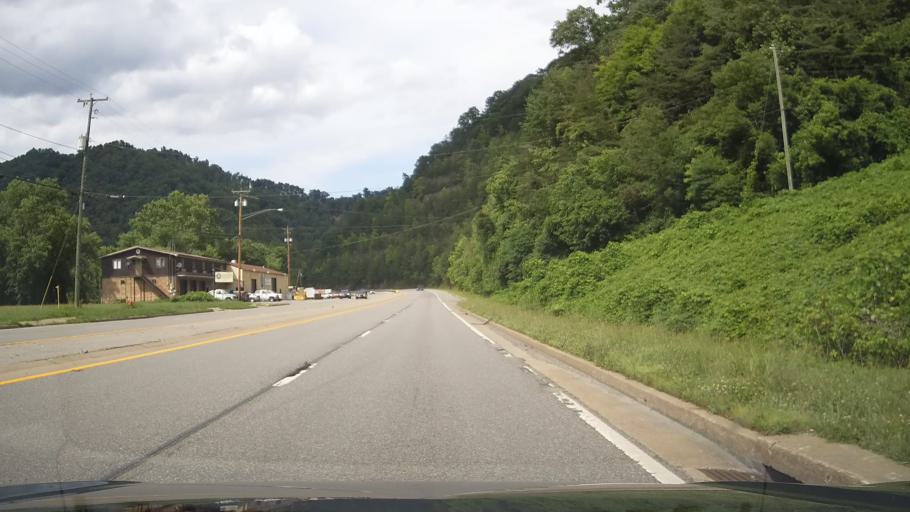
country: US
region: Kentucky
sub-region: Pike County
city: Pikeville
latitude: 37.4556
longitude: -82.5198
